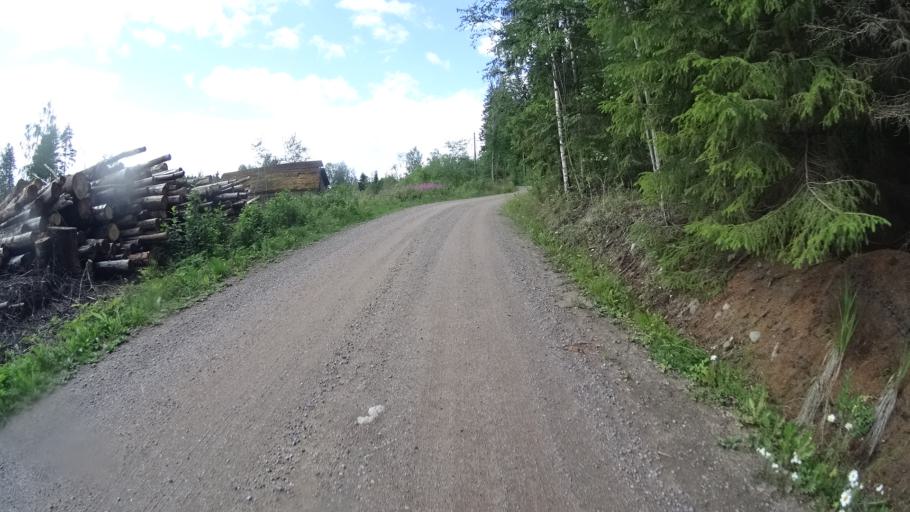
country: FI
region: Uusimaa
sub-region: Helsinki
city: Karkkila
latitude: 60.5957
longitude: 24.2205
